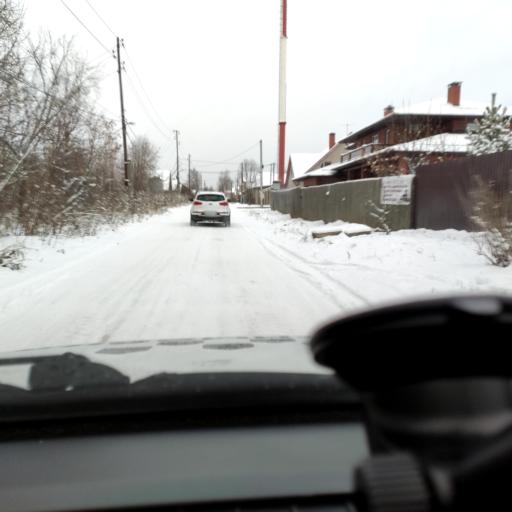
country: RU
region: Perm
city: Perm
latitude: 58.0582
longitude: 56.3629
